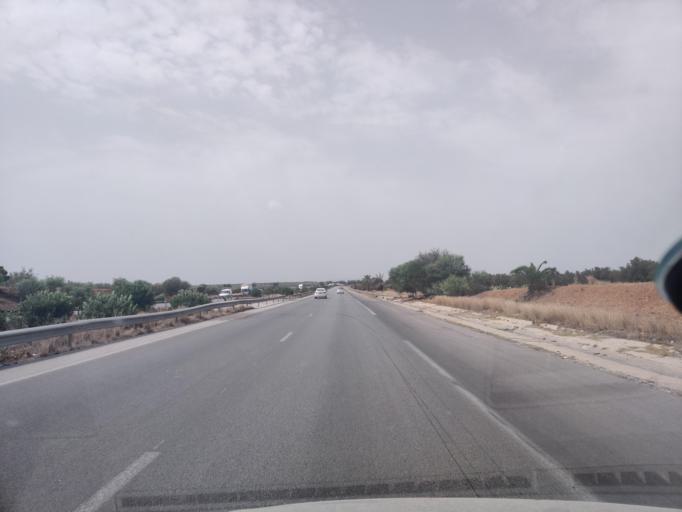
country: TN
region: Susah
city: Sidi Bou Ali
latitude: 35.9681
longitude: 10.4713
